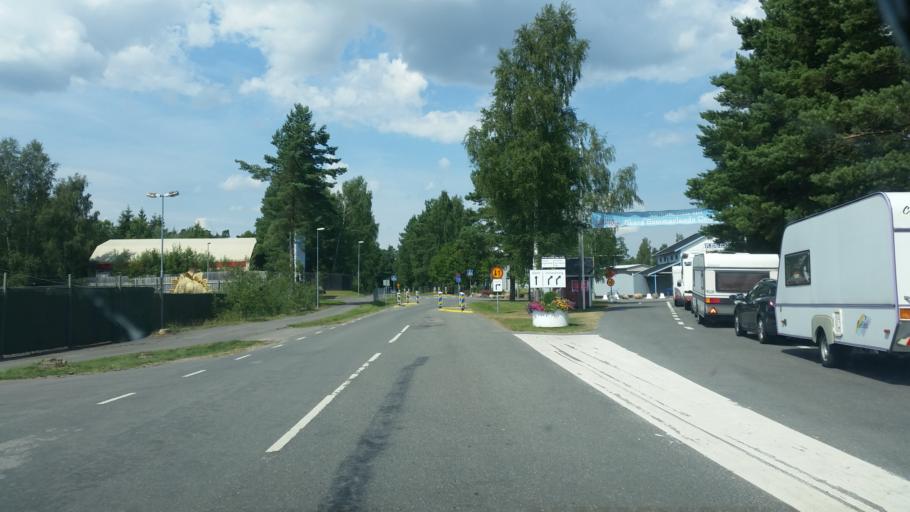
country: SE
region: Vaestra Goetaland
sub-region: Skara Kommun
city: Axvall
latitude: 58.4103
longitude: 13.5554
